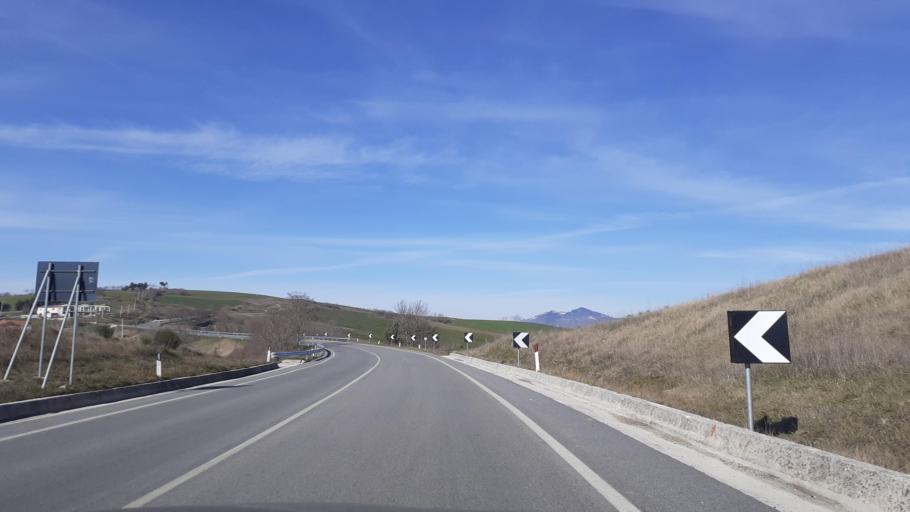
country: IT
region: Molise
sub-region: Provincia di Campobasso
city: Pietracupa
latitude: 41.6843
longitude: 14.5137
